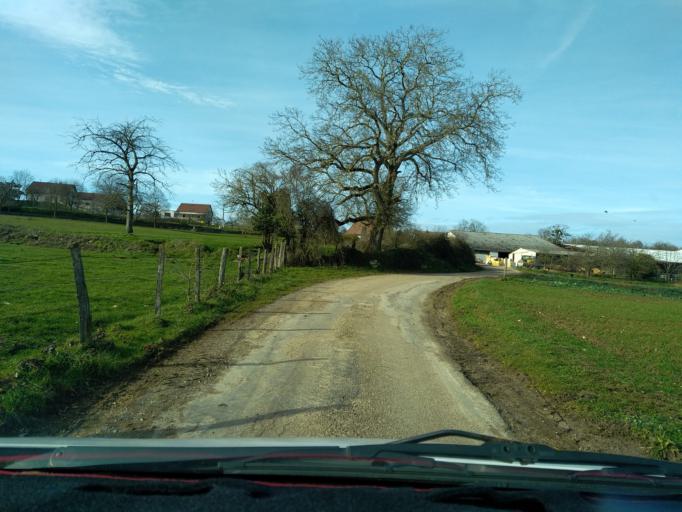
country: FR
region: Franche-Comte
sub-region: Departement de la Haute-Saone
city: Marnay
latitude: 47.3007
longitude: 5.6708
